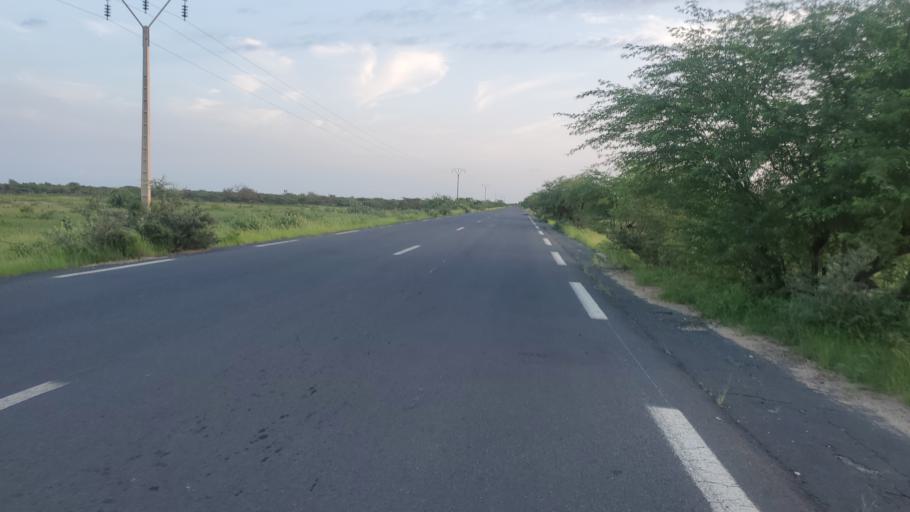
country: SN
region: Saint-Louis
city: Saint-Louis
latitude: 16.1289
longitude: -16.4128
